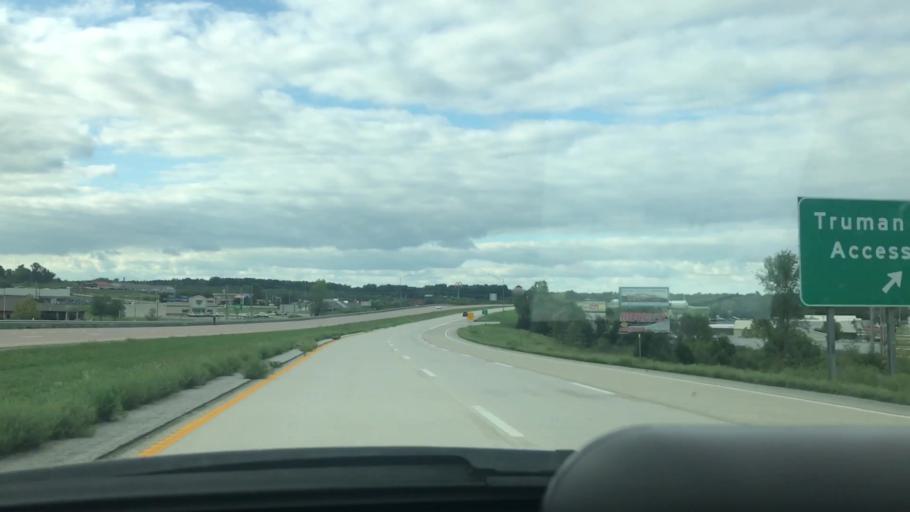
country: US
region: Missouri
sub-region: Benton County
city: Warsaw
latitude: 38.2602
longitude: -93.3660
